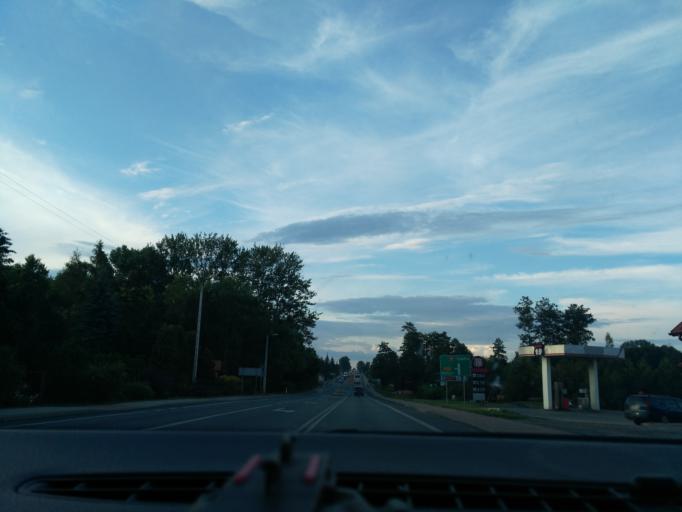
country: PL
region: Lublin Voivodeship
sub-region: Powiat lubelski
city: Niedrzwica Duza
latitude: 51.1147
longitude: 22.3891
